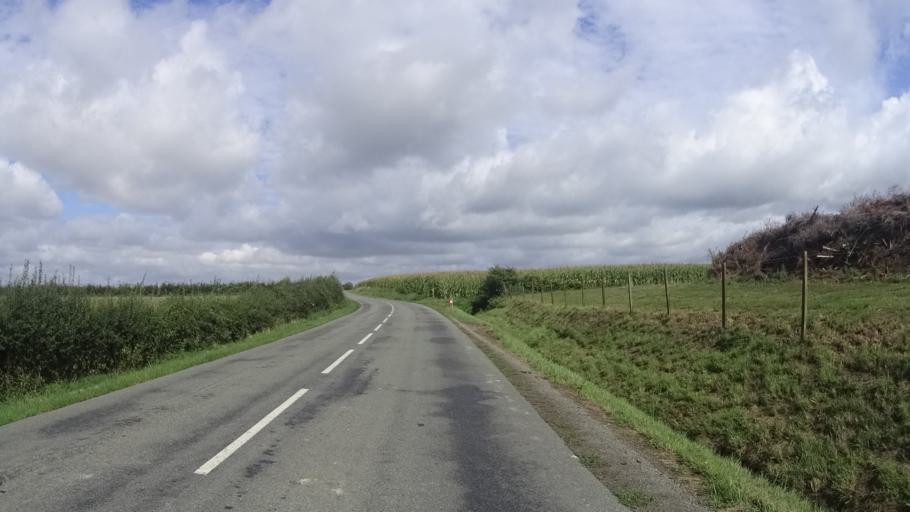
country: FR
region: Nord-Pas-de-Calais
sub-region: Departement du Nord
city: Landrecies
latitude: 50.0824
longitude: 3.6486
